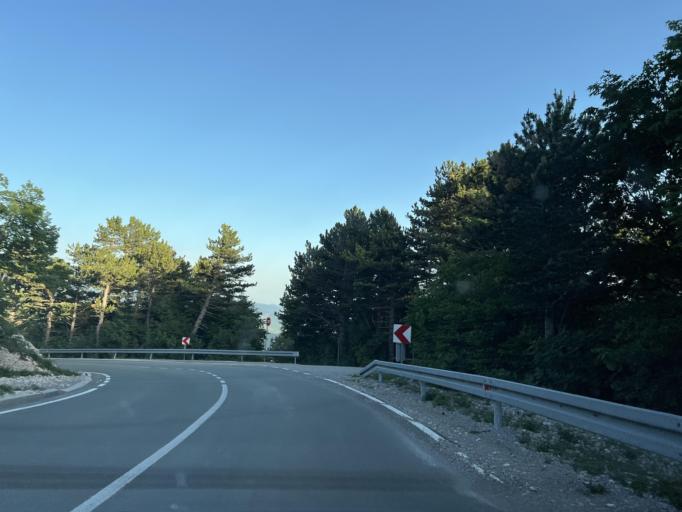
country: HR
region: Primorsko-Goranska
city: Podhum
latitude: 45.3975
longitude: 14.5488
